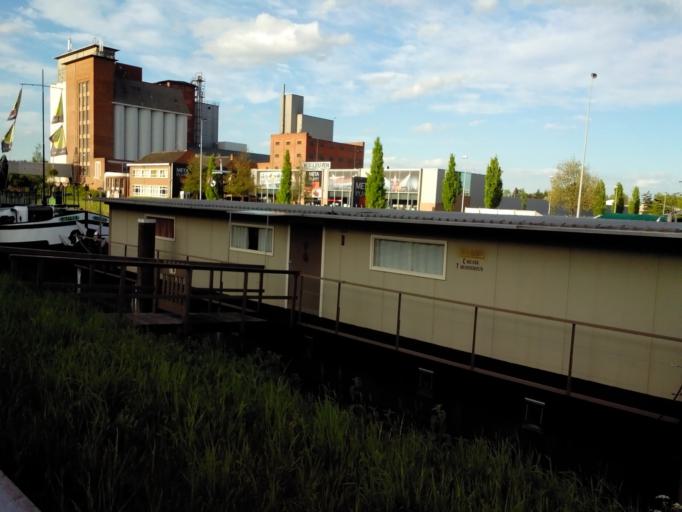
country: BE
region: Flanders
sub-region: Provincie Vlaams-Brabant
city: Leuven
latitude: 50.8897
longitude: 4.7062
